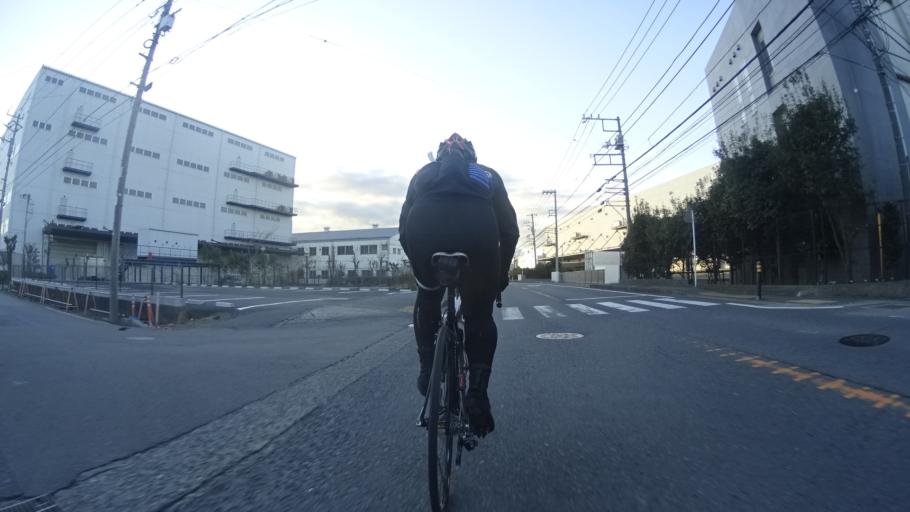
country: JP
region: Kanagawa
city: Atsugi
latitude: 35.4558
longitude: 139.3686
